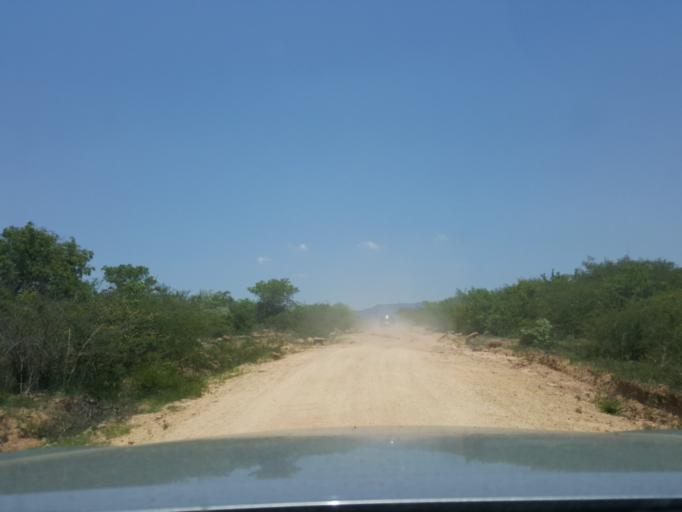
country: ZA
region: Limpopo
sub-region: Mopani District Municipality
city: Hoedspruit
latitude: -24.5764
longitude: 30.9948
